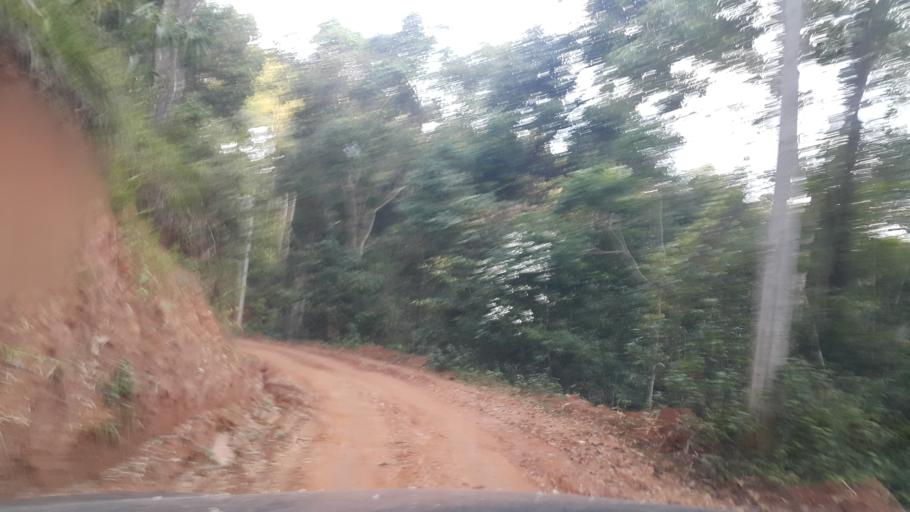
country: TH
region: Chiang Mai
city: Samoeng
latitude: 19.0071
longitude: 98.6611
